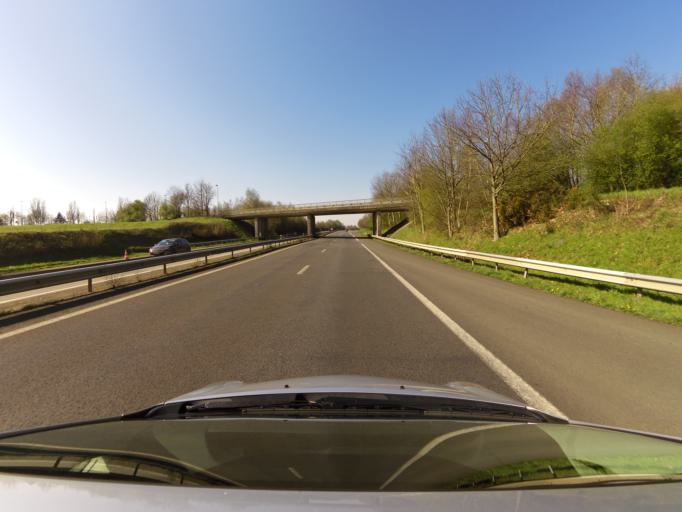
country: FR
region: Brittany
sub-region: Departement d'Ille-et-Vilaine
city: Le Rheu
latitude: 48.0797
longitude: -1.7932
